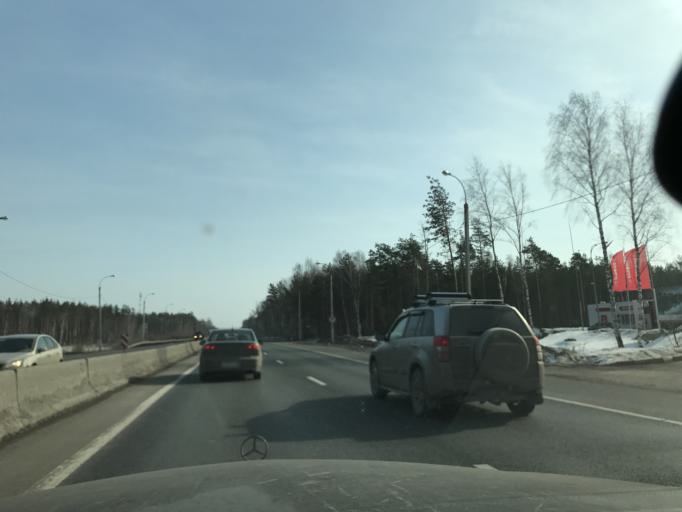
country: RU
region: Nizjnij Novgorod
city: Pyra
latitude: 56.2938
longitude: 43.3659
